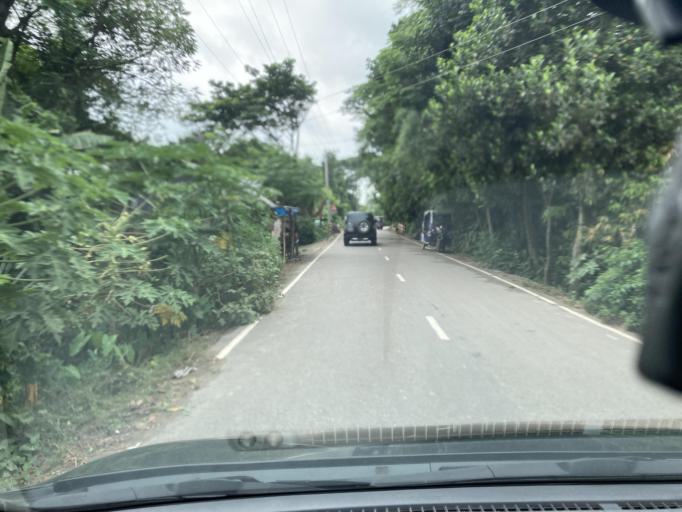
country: BD
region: Dhaka
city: Azimpur
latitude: 23.7710
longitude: 90.2051
